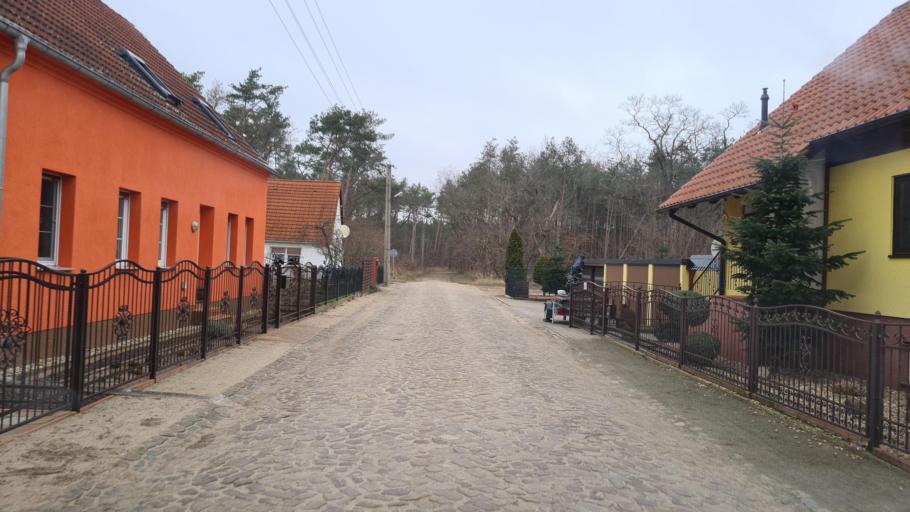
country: DE
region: Brandenburg
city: Herzberg
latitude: 51.6853
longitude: 13.1861
